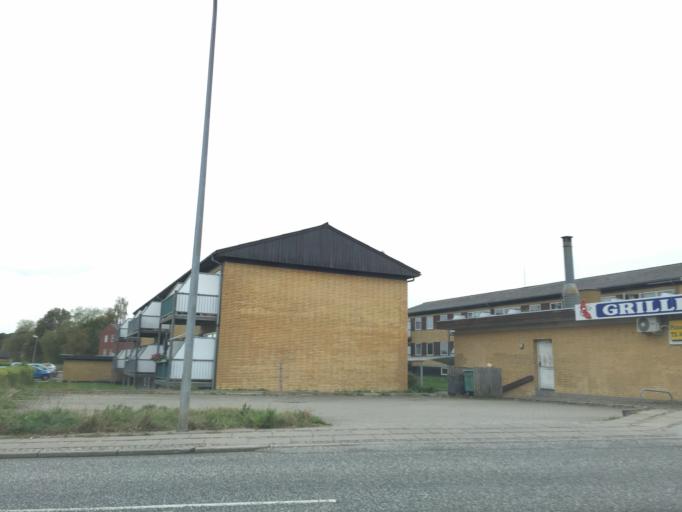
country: DK
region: Central Jutland
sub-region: Viborg Kommune
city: Bjerringbro
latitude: 56.3806
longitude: 9.6643
